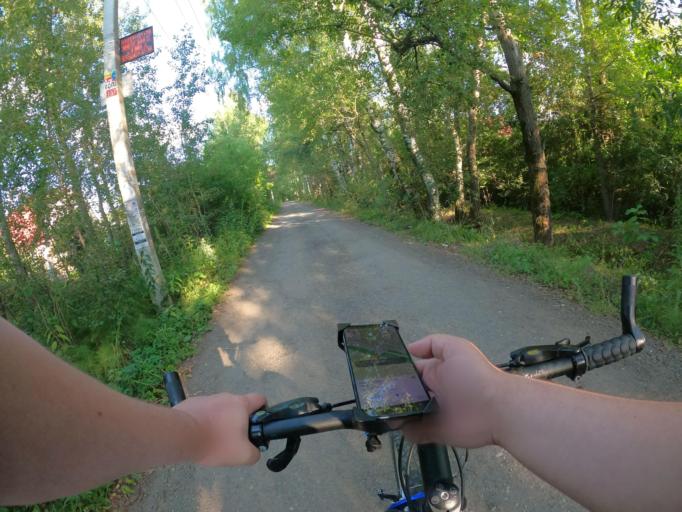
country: RU
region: Moskovskaya
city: Beloozerskiy
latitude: 55.4825
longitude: 38.4149
